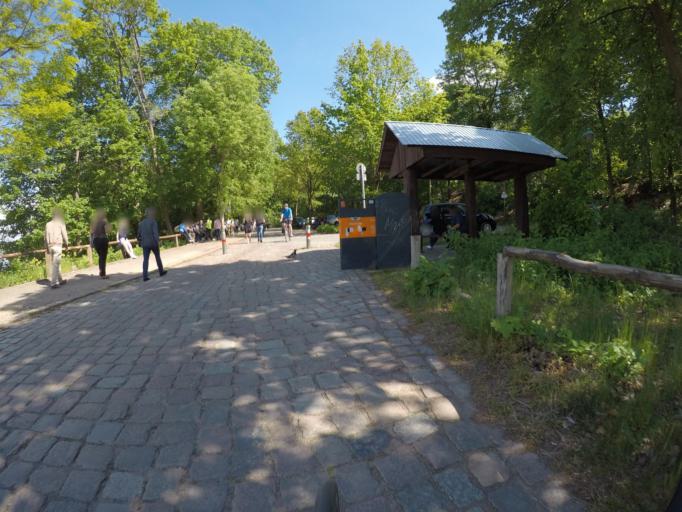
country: DE
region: Berlin
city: Kladow
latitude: 52.4284
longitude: 13.1232
